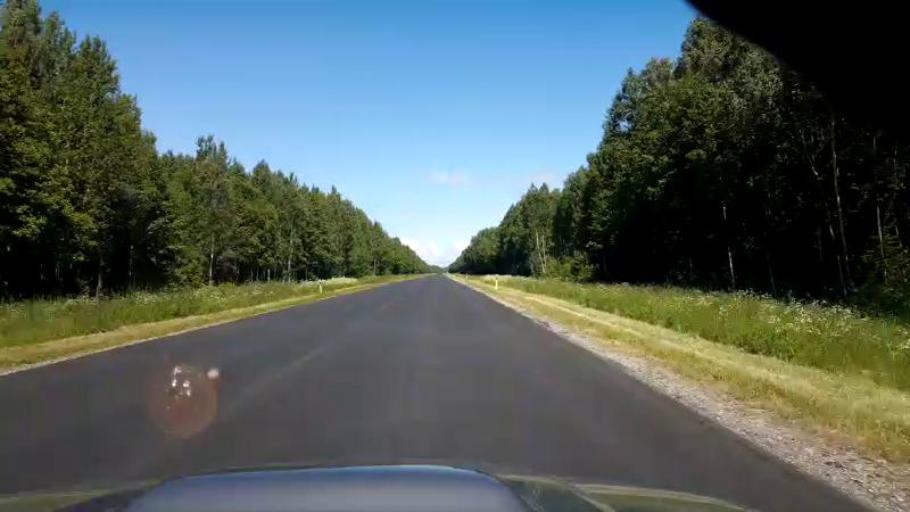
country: LV
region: Salacgrivas
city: Ainazi
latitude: 57.9202
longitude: 24.4225
